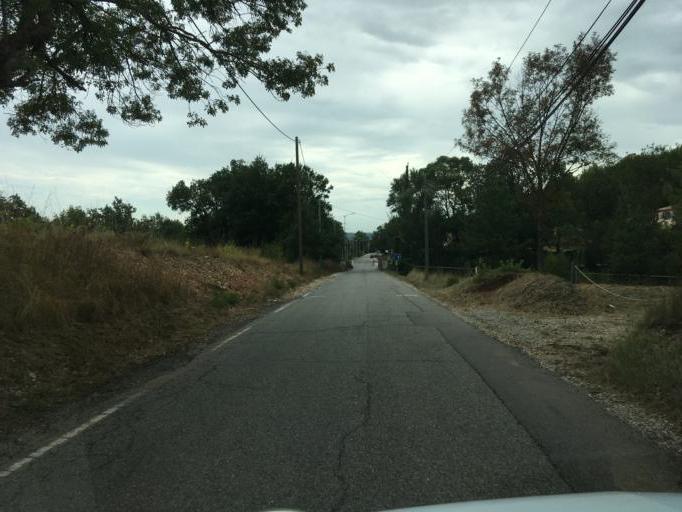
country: FR
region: Provence-Alpes-Cote d'Azur
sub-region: Departement des Bouches-du-Rhone
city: Rousset
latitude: 43.4873
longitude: 5.6289
